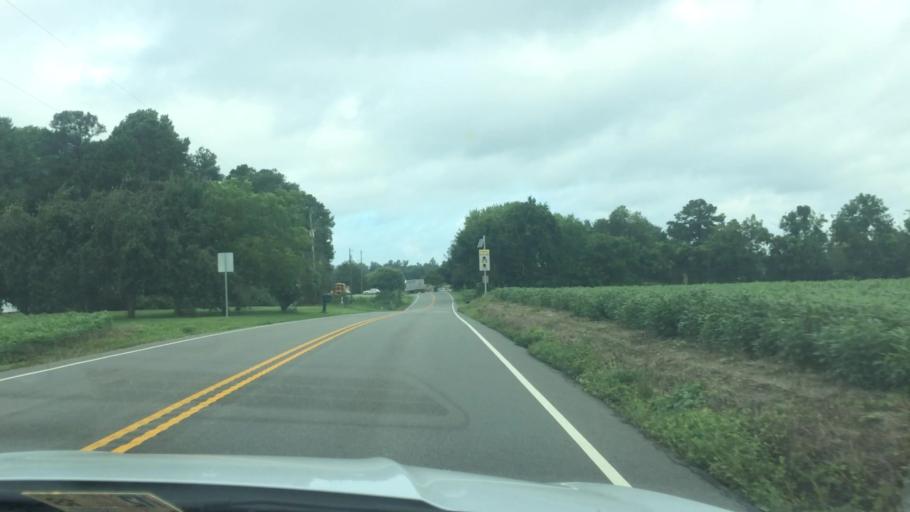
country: US
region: Virginia
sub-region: King William County
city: West Point
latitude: 37.6111
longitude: -76.7813
